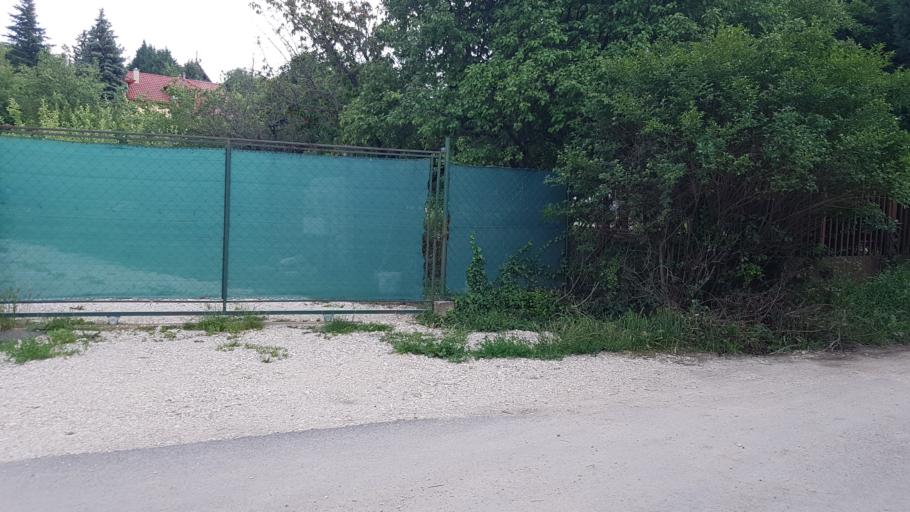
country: HU
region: Pest
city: Budakalasz
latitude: 47.6128
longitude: 19.0452
